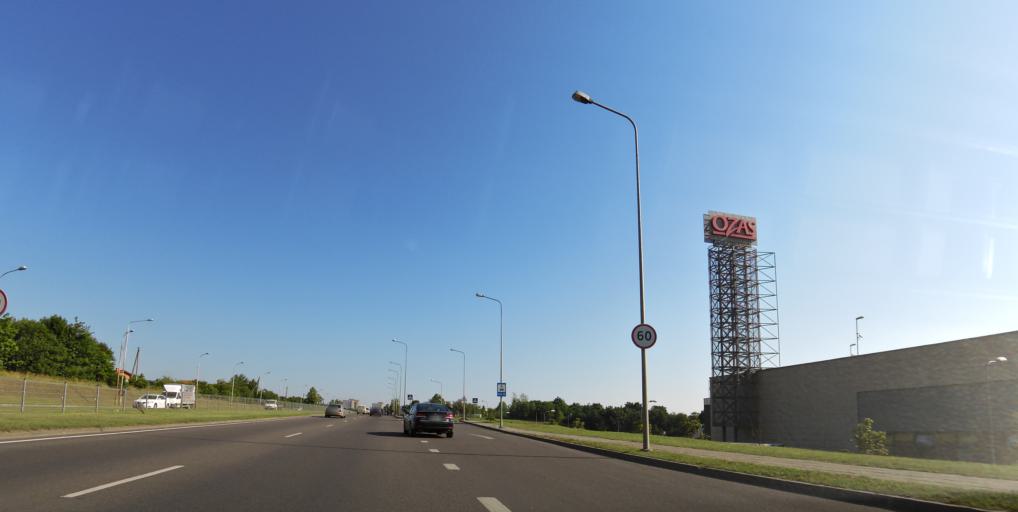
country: LT
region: Vilnius County
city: Seskine
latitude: 54.7140
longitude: 25.2709
